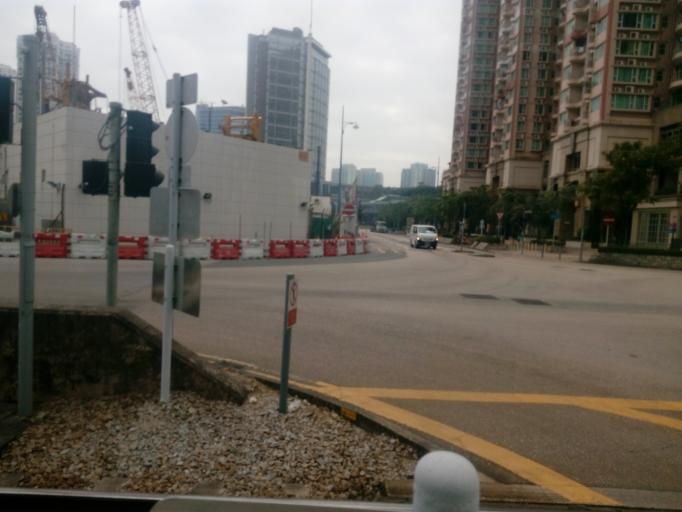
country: HK
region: Yuen Long
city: Yuen Long Kau Hui
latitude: 22.4604
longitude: 114.0014
